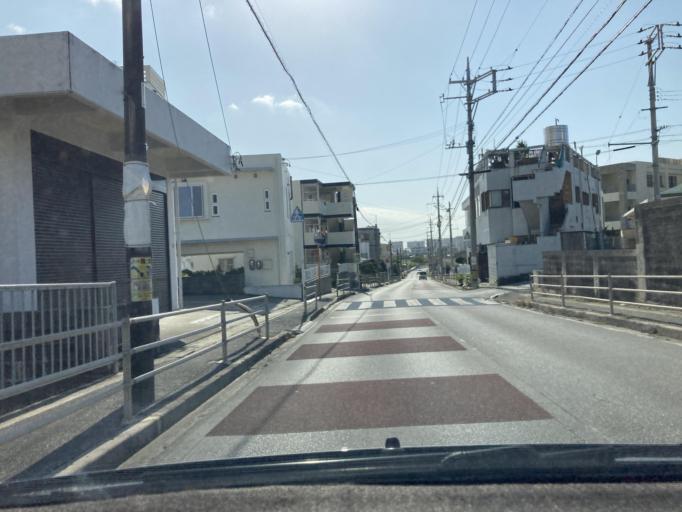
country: JP
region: Okinawa
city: Tomigusuku
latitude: 26.1662
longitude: 127.6745
